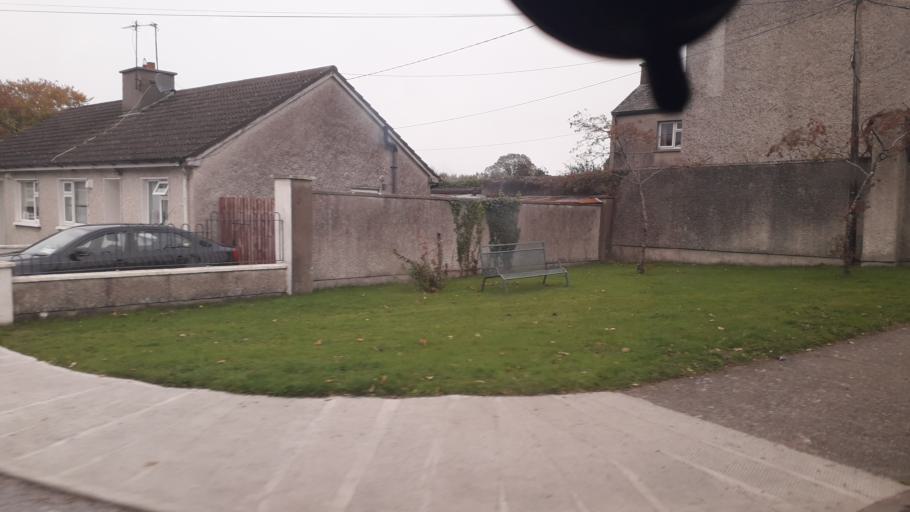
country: IE
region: Leinster
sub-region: Uibh Fhaili
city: Birr
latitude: 52.9827
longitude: -7.9294
